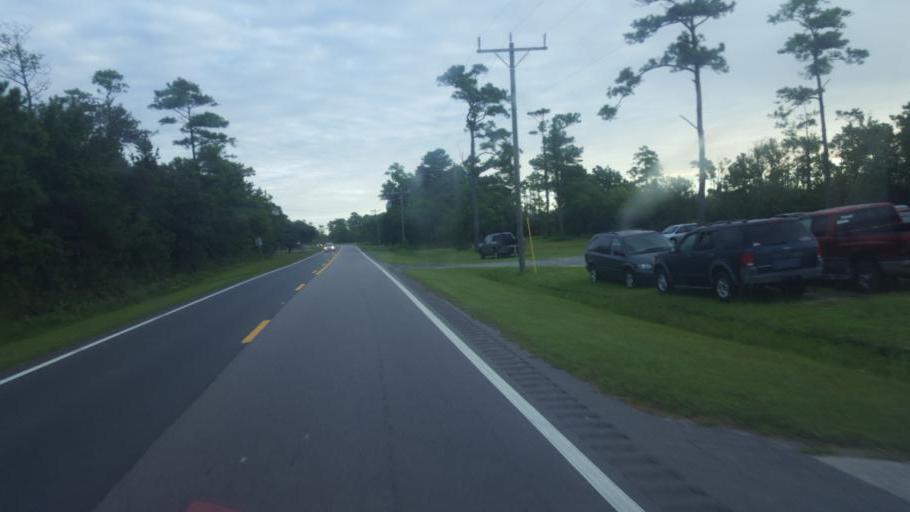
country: US
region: North Carolina
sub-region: Dare County
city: Manteo
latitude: 35.8833
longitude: -75.6591
